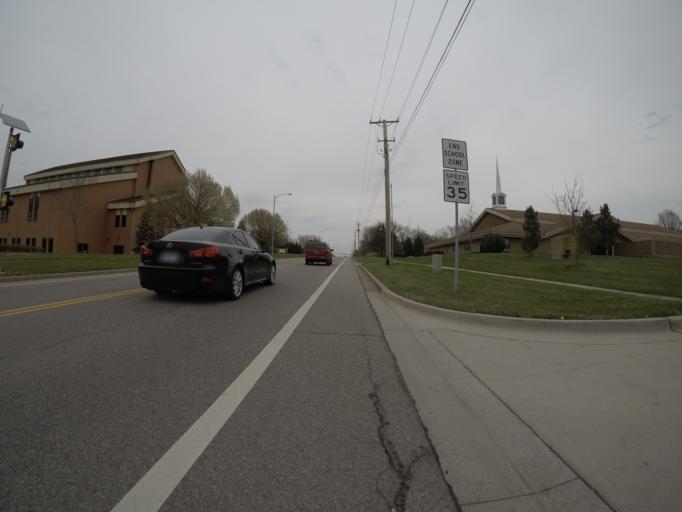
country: US
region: Kansas
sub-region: Johnson County
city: Olathe
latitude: 38.8691
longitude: -94.7717
